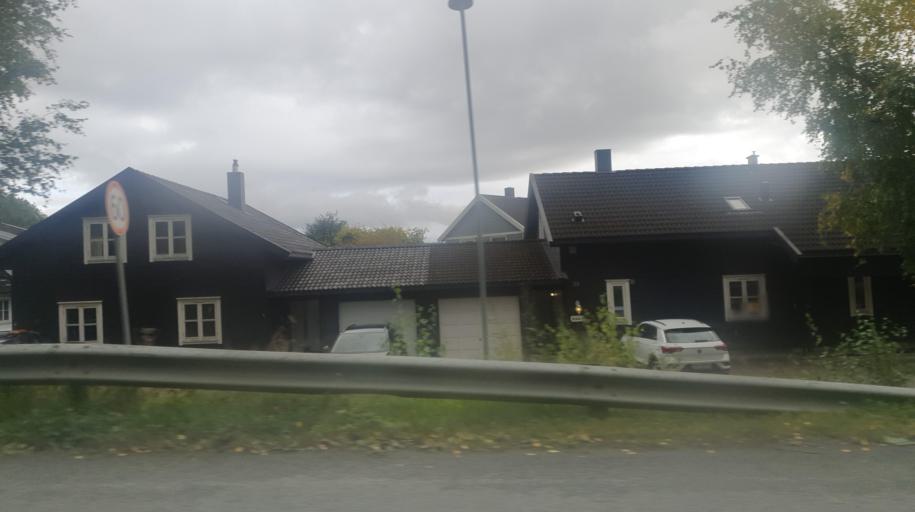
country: NO
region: Nord-Trondelag
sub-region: Verdal
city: Verdal
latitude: 63.7957
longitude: 11.5104
